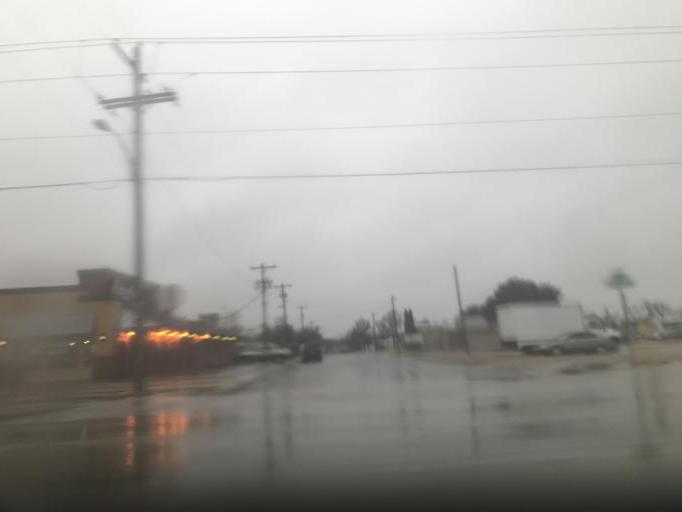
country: US
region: Texas
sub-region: Tom Green County
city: San Angelo
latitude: 31.4708
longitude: -100.4114
